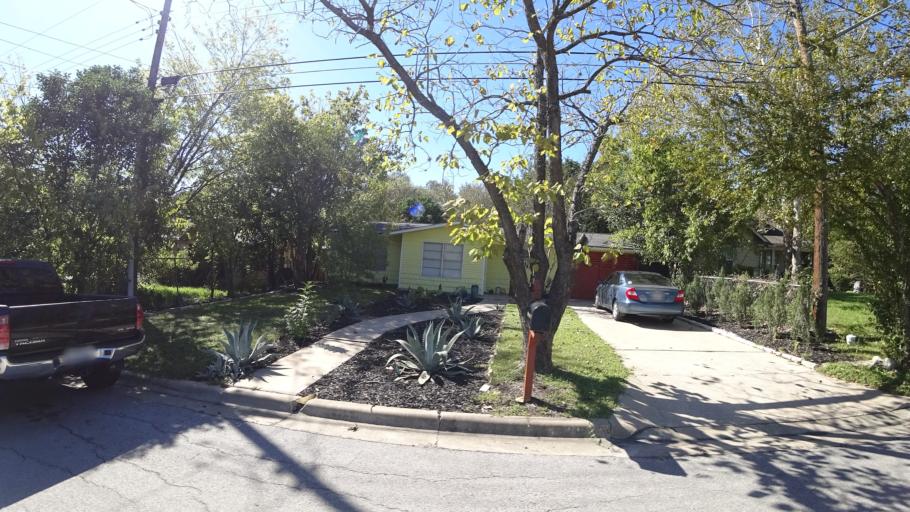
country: US
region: Texas
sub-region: Travis County
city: Austin
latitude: 30.2807
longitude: -97.6825
